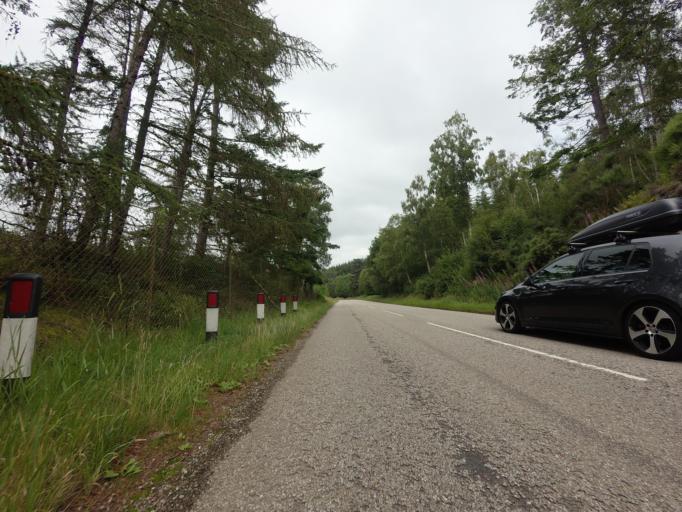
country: GB
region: Scotland
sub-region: Highland
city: Alness
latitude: 57.9057
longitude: -4.3602
